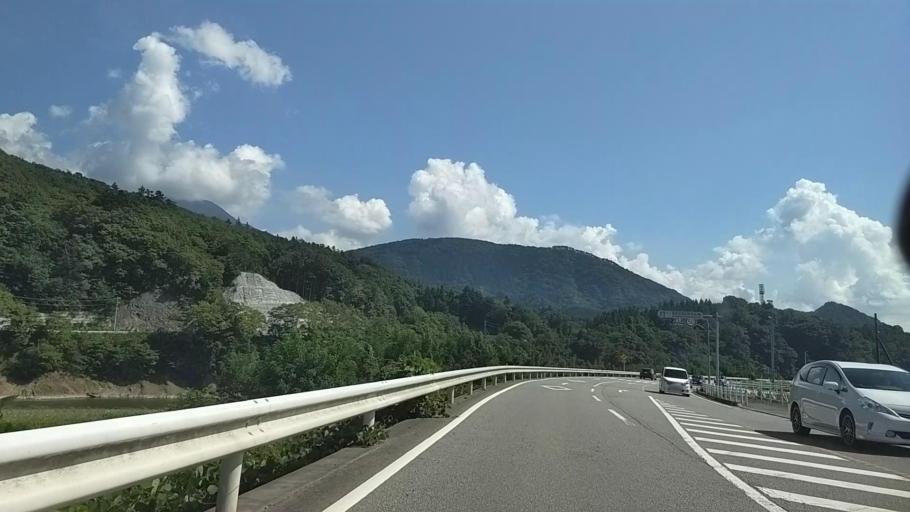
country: JP
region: Yamanashi
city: Ryuo
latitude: 35.4547
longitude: 138.4461
